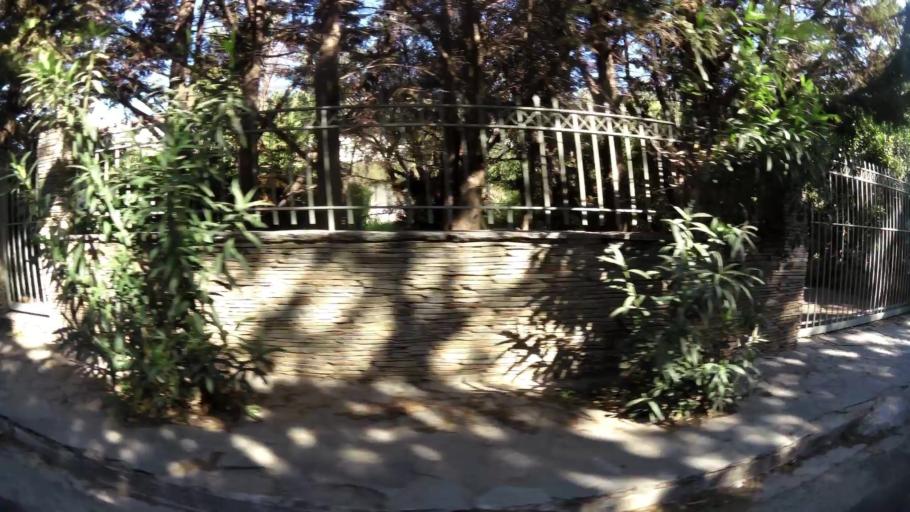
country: GR
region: Attica
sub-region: Nomarchia Anatolikis Attikis
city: Pikermi
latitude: 38.0052
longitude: 23.9390
